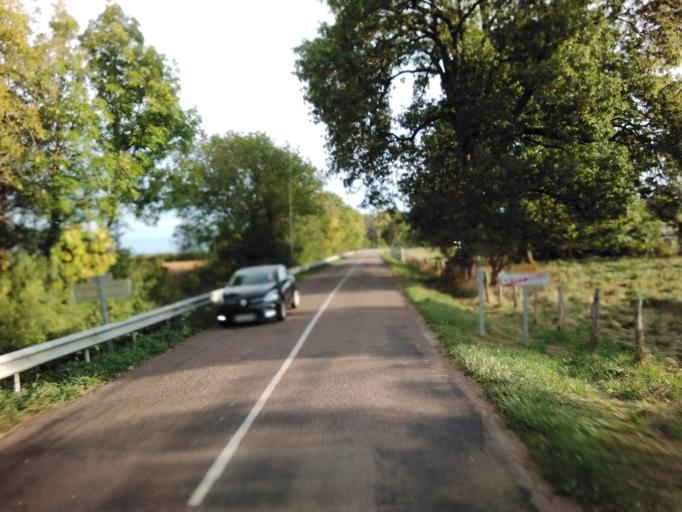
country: FR
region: Champagne-Ardenne
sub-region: Departement de l'Aube
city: Les Riceys
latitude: 47.8689
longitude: 4.3544
